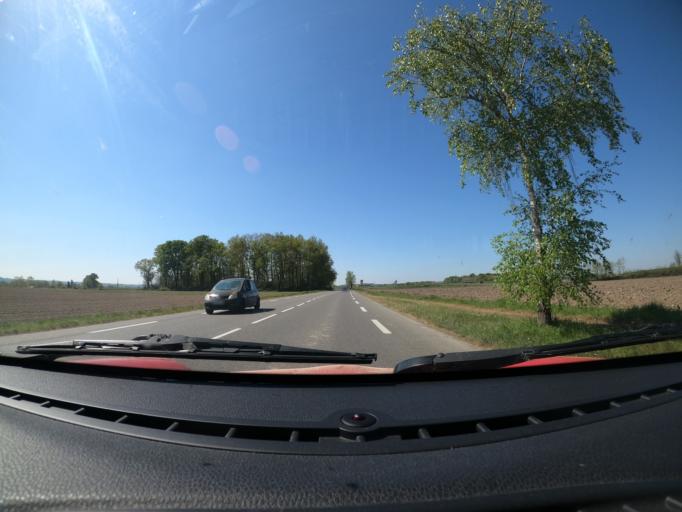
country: FR
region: Aquitaine
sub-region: Departement des Pyrenees-Atlantiques
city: Lescar
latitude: 43.3423
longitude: -0.4108
